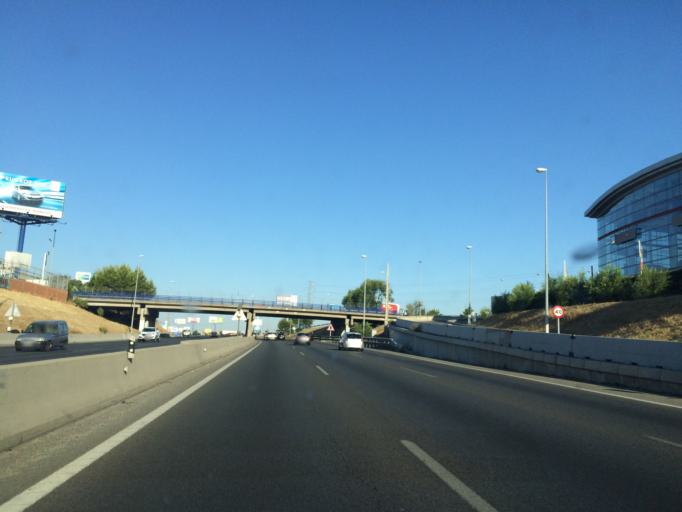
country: ES
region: Madrid
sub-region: Provincia de Madrid
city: Alcorcon
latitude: 40.3544
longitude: -3.8278
